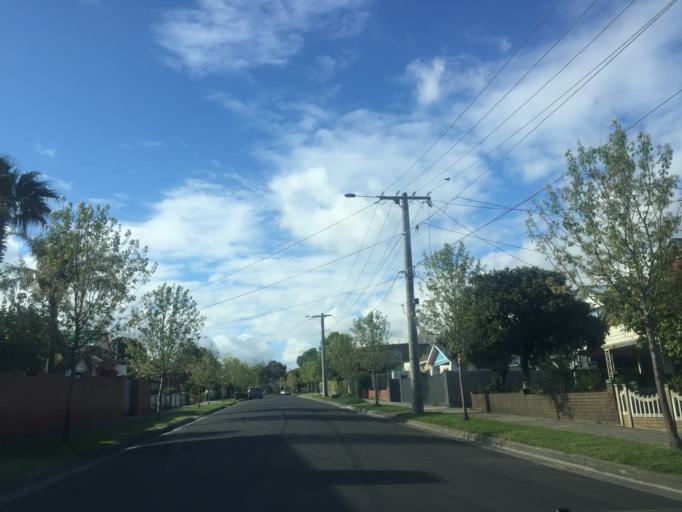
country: AU
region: Victoria
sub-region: Darebin
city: Reservoir
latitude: -37.7294
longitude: 145.0078
